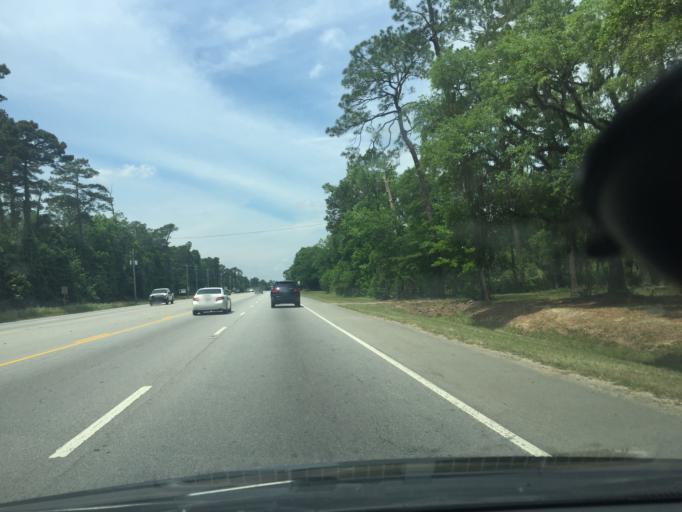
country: US
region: Georgia
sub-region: Chatham County
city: Bloomingdale
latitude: 32.1407
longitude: -81.3245
